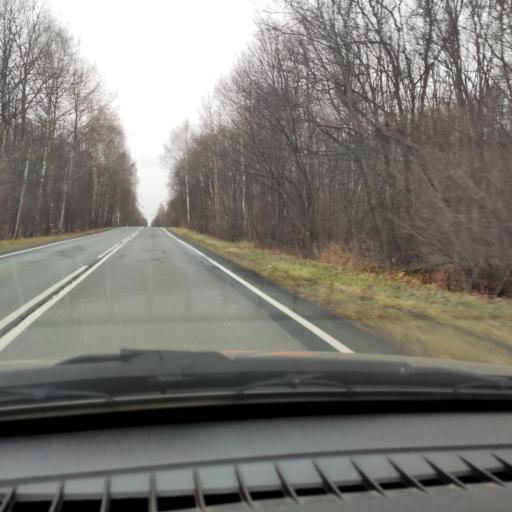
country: RU
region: Samara
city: Zhigulevsk
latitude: 53.3464
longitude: 49.5644
